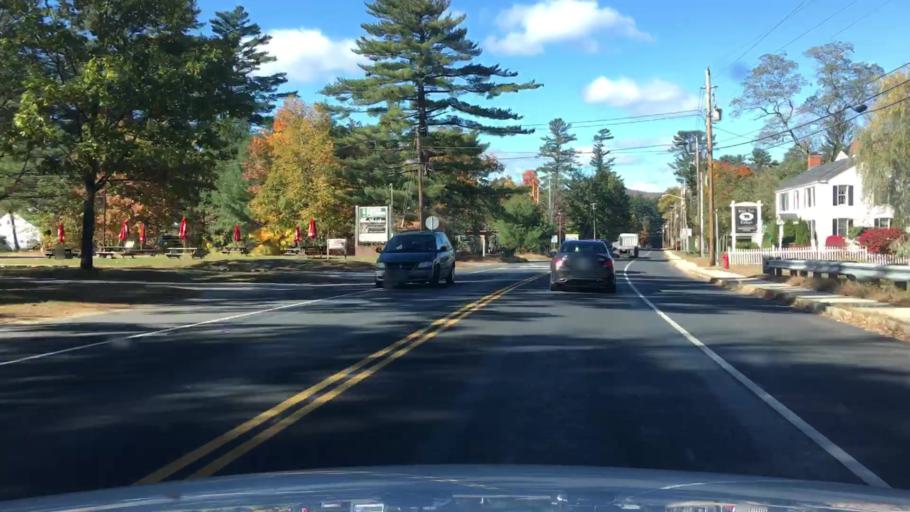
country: US
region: New Hampshire
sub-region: Carroll County
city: North Conway
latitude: 44.0570
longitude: -71.1325
